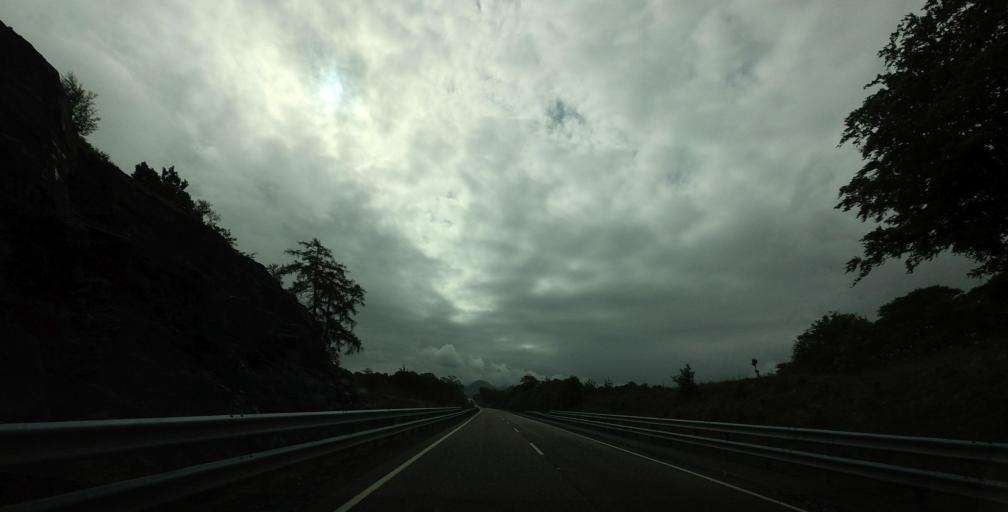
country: GB
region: Scotland
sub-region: Argyll and Bute
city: Isle Of Mull
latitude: 56.9056
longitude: -5.8181
